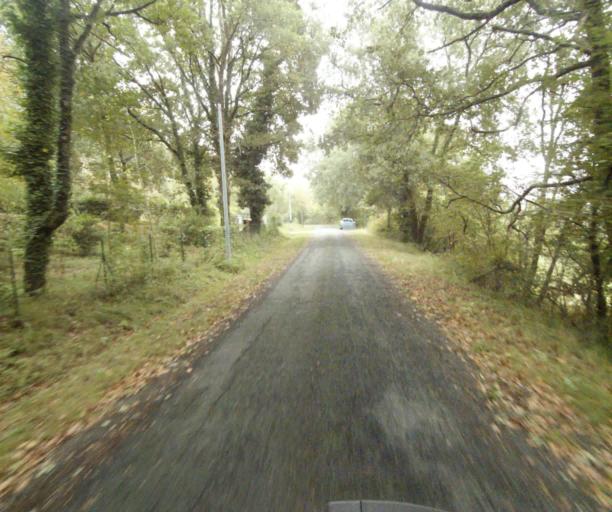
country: FR
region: Midi-Pyrenees
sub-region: Departement de la Haute-Garonne
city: Villemur-sur-Tarn
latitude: 43.8909
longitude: 1.4819
